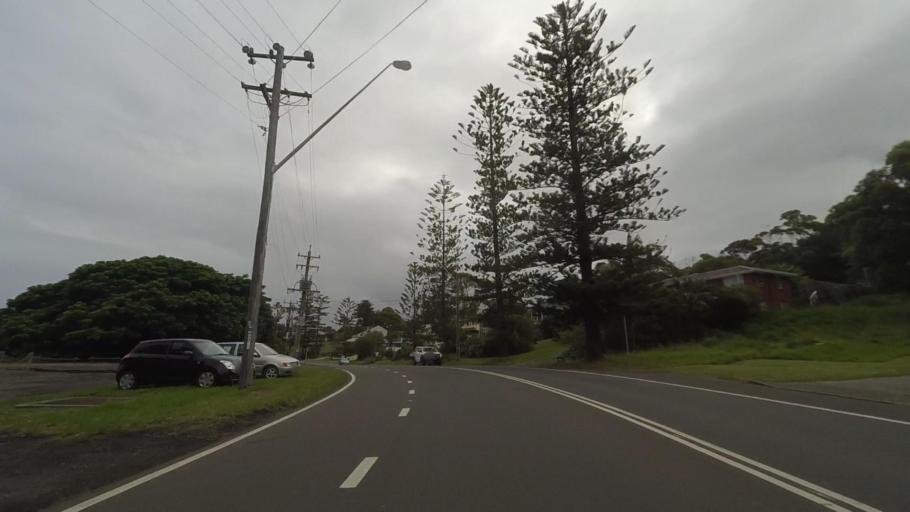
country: AU
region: New South Wales
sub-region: Wollongong
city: Bulli
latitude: -34.2966
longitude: 150.9411
